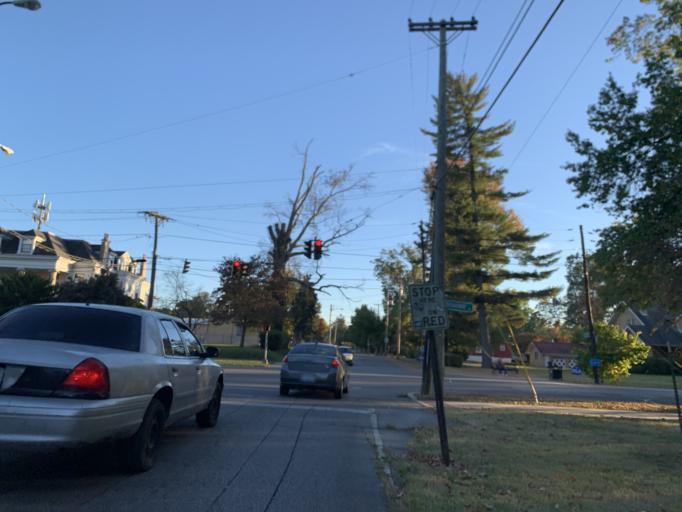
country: US
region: Indiana
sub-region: Floyd County
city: New Albany
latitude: 38.2508
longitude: -85.8270
